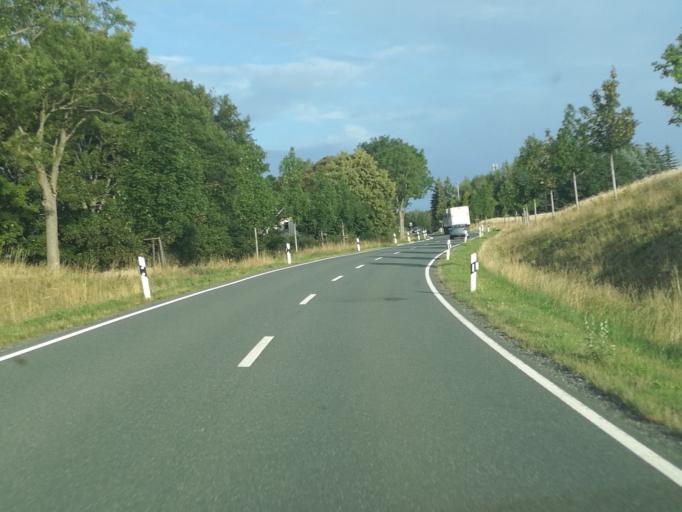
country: DE
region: Saxony
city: Adorf
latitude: 50.3331
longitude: 12.2279
